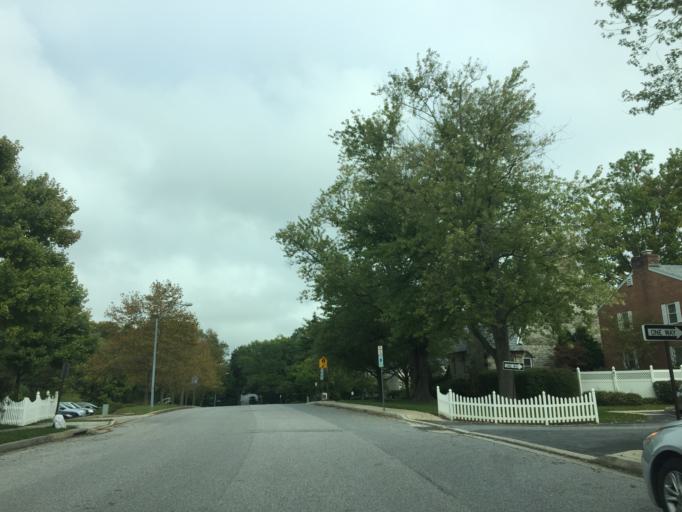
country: US
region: Maryland
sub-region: Baltimore County
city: Reisterstown
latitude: 39.4700
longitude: -76.8218
